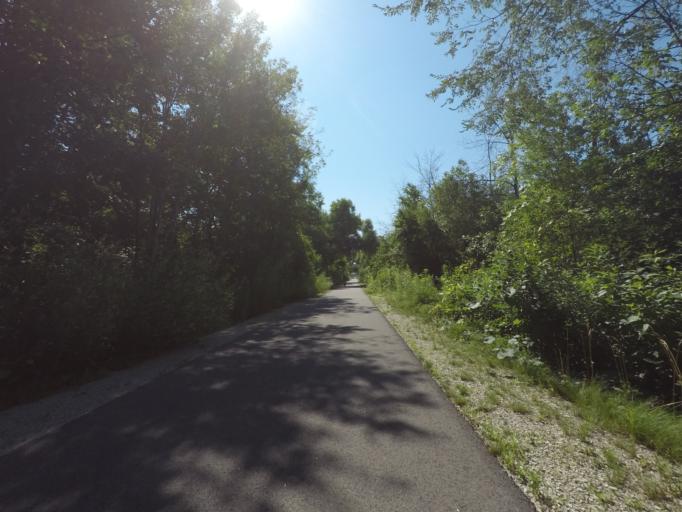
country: US
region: Wisconsin
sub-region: Waukesha County
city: Elm Grove
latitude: 43.0325
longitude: -88.0605
